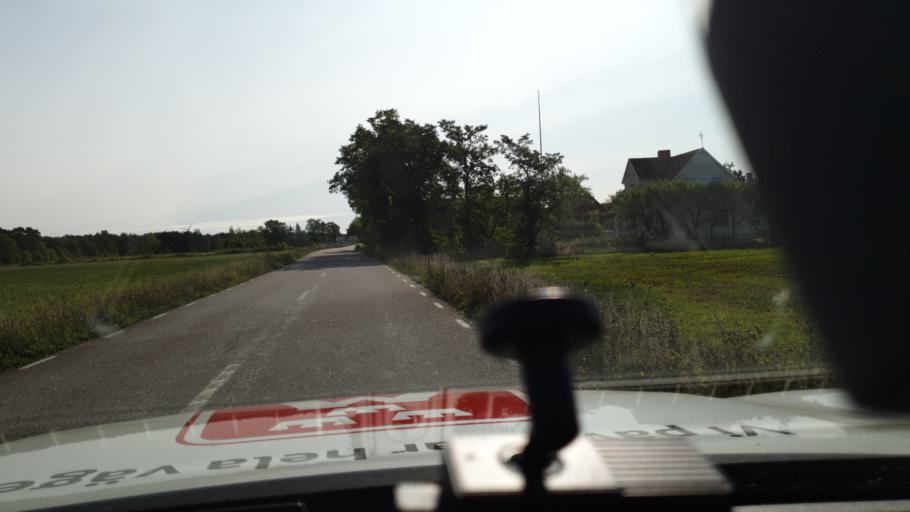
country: SE
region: Gotland
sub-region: Gotland
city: Hemse
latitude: 57.1132
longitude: 18.2832
